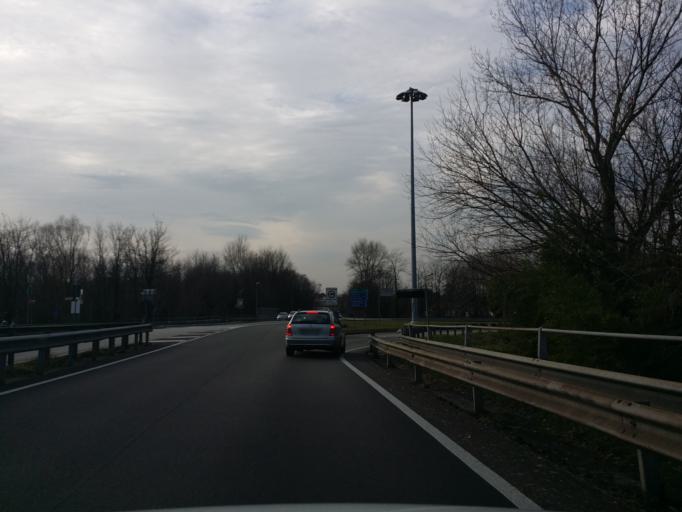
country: IT
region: Veneto
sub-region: Provincia di Padova
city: Padova
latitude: 45.4107
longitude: 11.8540
